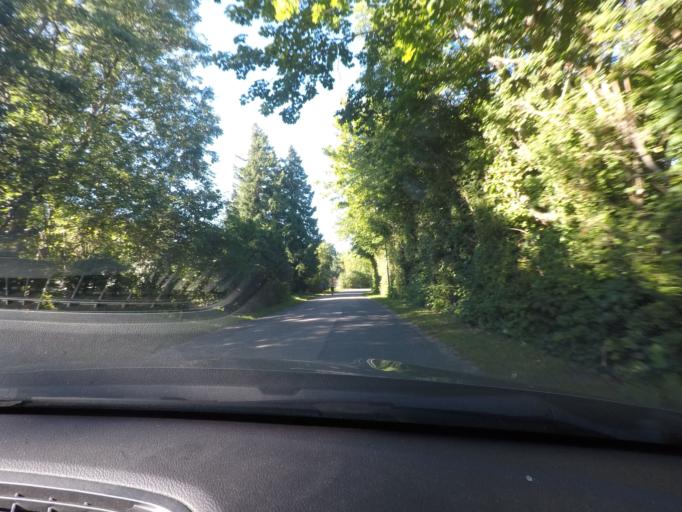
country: DK
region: Zealand
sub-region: Guldborgsund Kommune
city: Sakskobing
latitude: 54.9804
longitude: 11.5300
